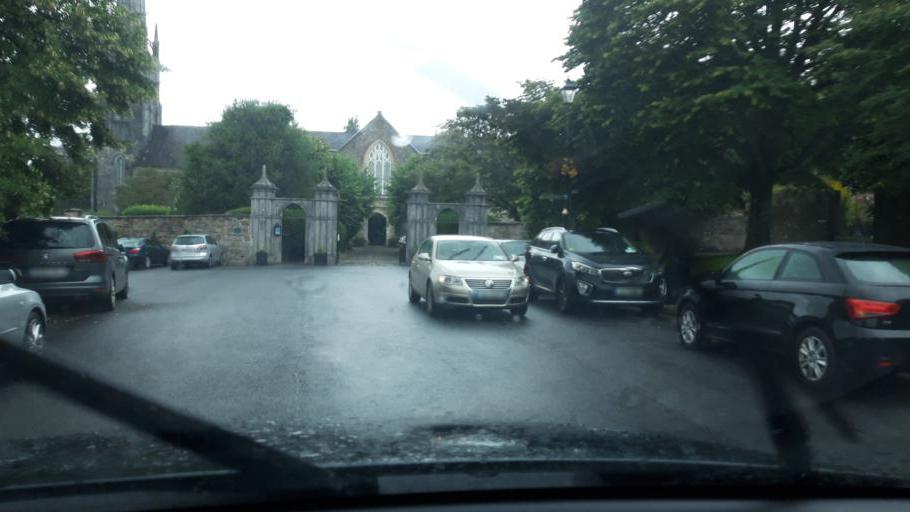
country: IE
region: Munster
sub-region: County Cork
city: Youghal
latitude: 52.1390
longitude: -7.9295
